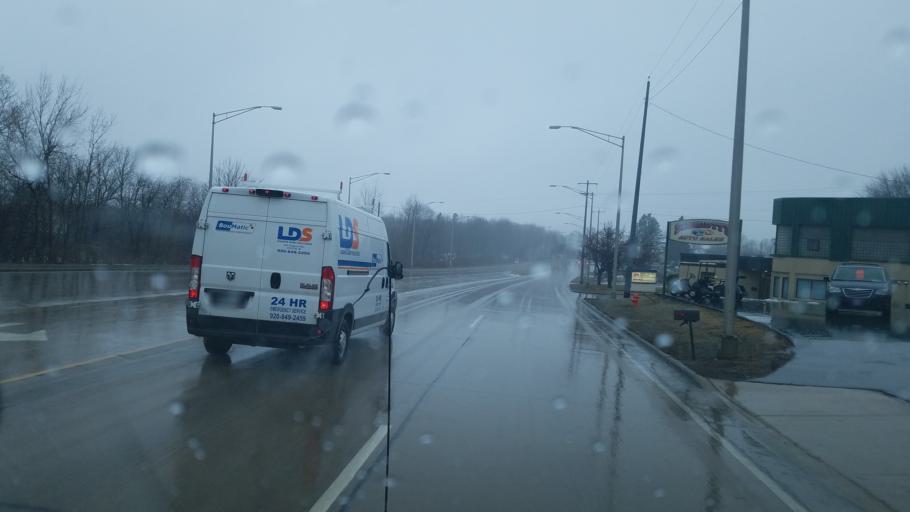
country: US
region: Wisconsin
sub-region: Wood County
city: Marshfield
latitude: 44.6735
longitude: -90.1867
